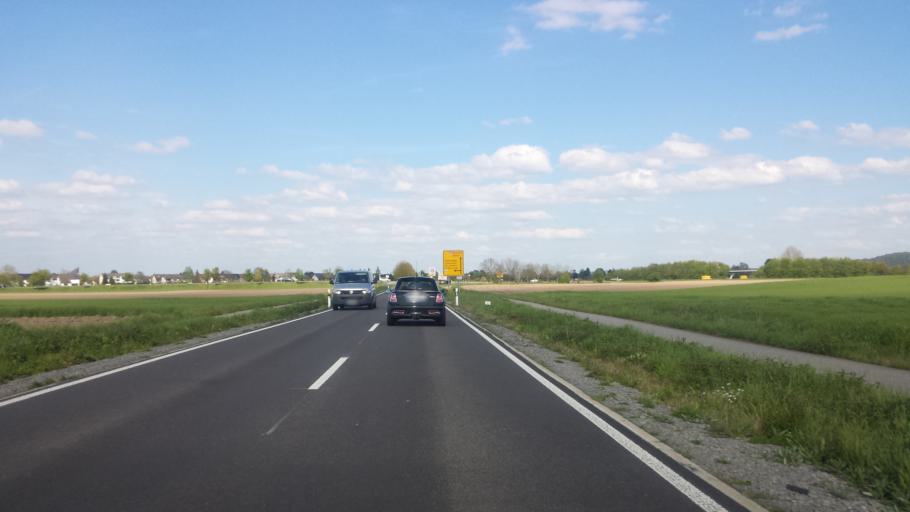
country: DE
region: Baden-Wuerttemberg
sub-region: Karlsruhe Region
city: Karlsdorf-Neuthard
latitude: 49.1040
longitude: 8.4988
